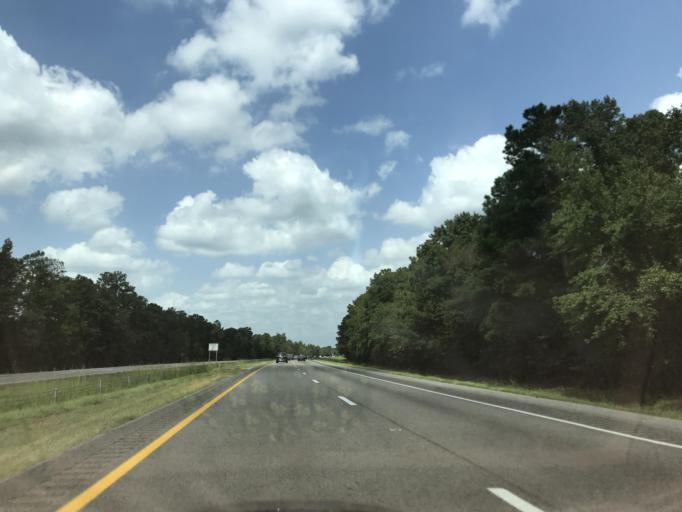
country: US
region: North Carolina
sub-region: Pender County
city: Burgaw
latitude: 34.6272
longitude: -77.9346
